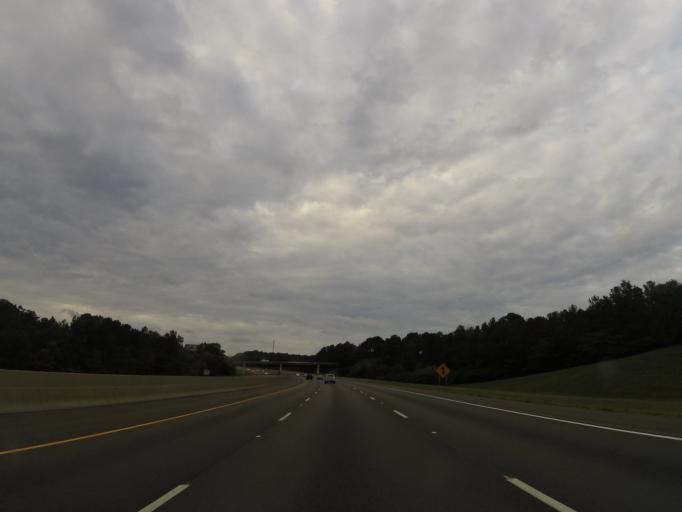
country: US
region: Alabama
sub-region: Jefferson County
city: Trussville
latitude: 33.5733
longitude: -86.6381
